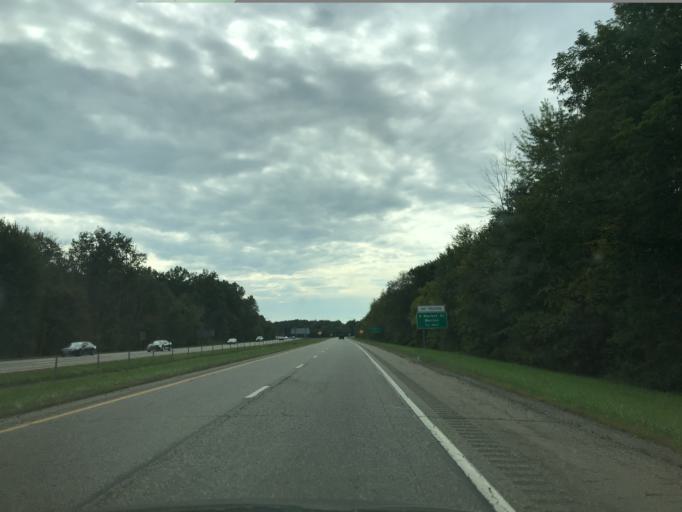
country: US
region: Ohio
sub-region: Trumbull County
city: Howland Center
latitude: 41.2476
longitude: -80.7659
